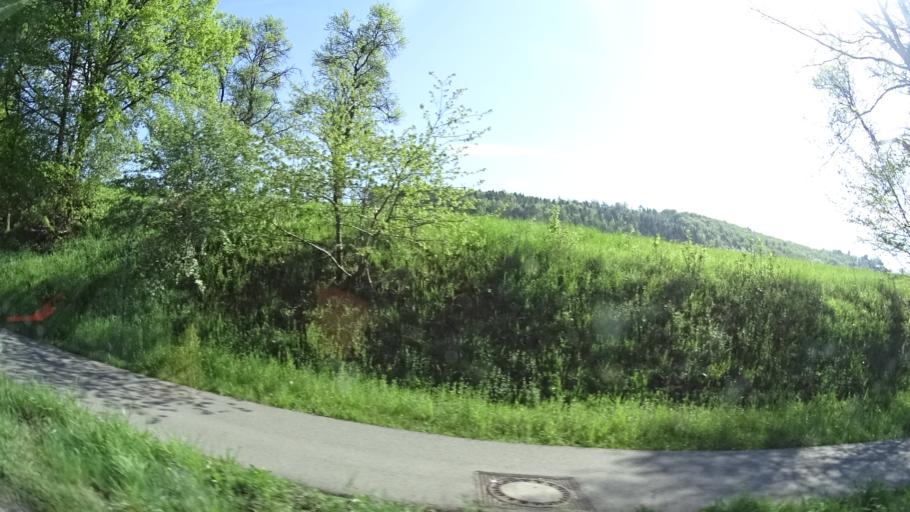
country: DE
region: Baden-Wuerttemberg
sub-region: Karlsruhe Region
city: Rohrdorf
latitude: 48.5559
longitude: 8.7050
